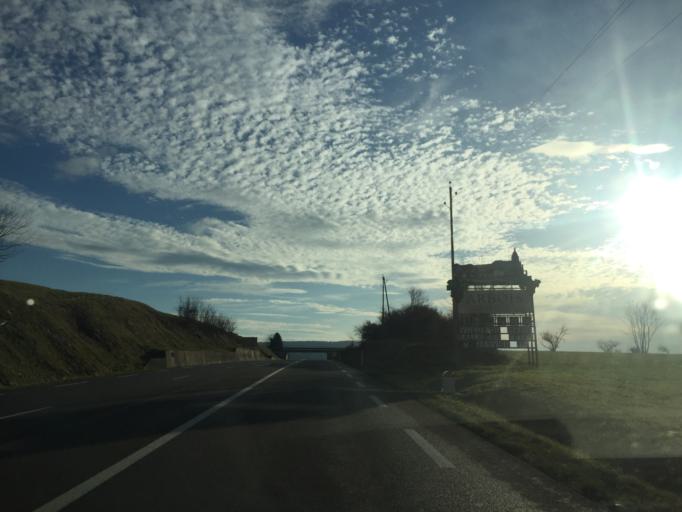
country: FR
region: Franche-Comte
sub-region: Departement du Jura
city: Arbois
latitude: 46.9317
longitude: 5.7759
